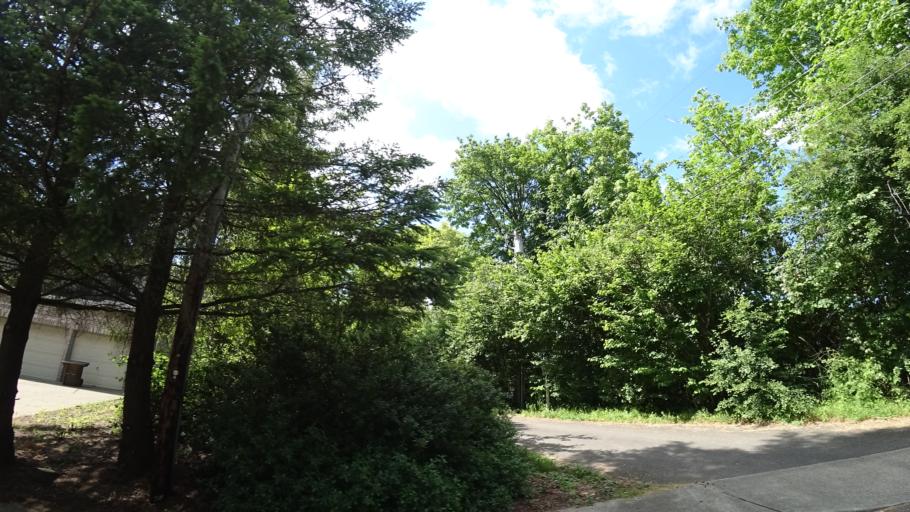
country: US
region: Oregon
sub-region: Washington County
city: Garden Home-Whitford
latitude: 45.4812
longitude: -122.7112
